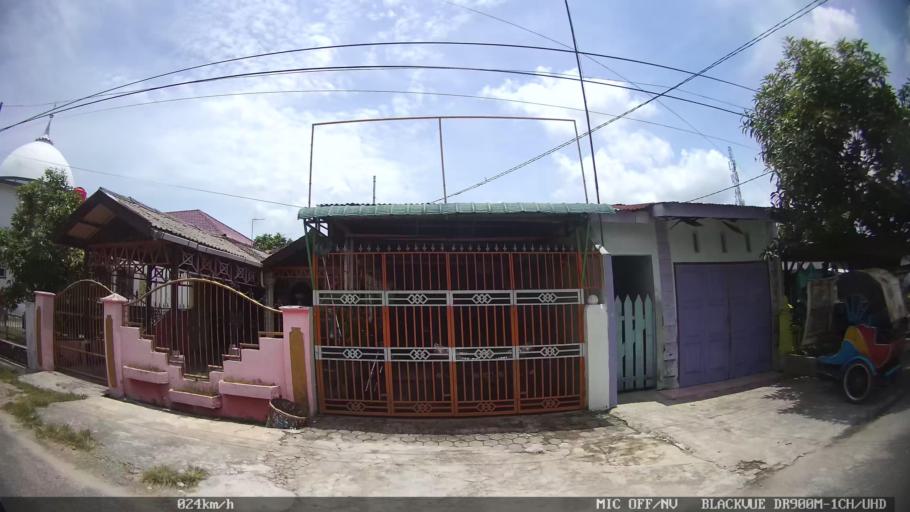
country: ID
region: North Sumatra
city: Percut
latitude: 3.5569
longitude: 98.8698
